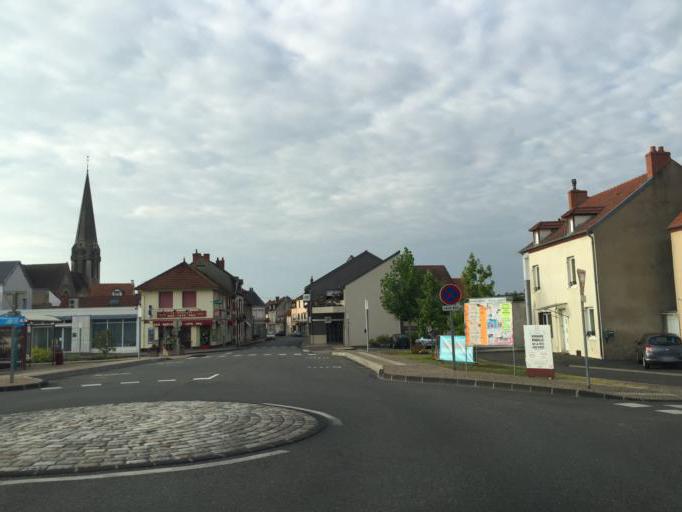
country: FR
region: Auvergne
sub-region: Departement de l'Allier
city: Saint-Germain-des-Fosses
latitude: 46.2019
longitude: 3.4334
